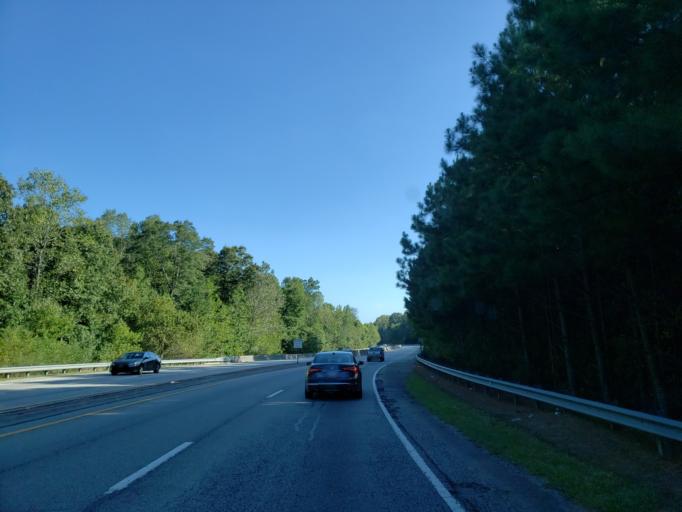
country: US
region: Georgia
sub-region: Cobb County
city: Powder Springs
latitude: 33.9201
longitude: -84.6289
